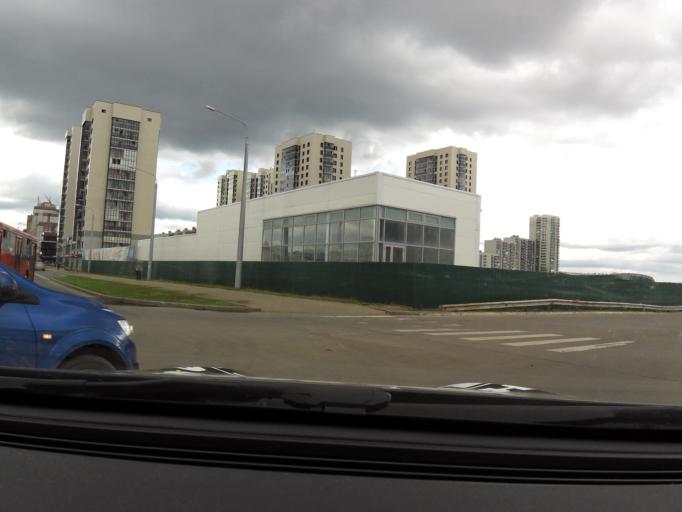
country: RU
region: Tatarstan
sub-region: Gorod Kazan'
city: Kazan
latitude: 55.8128
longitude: 49.1342
